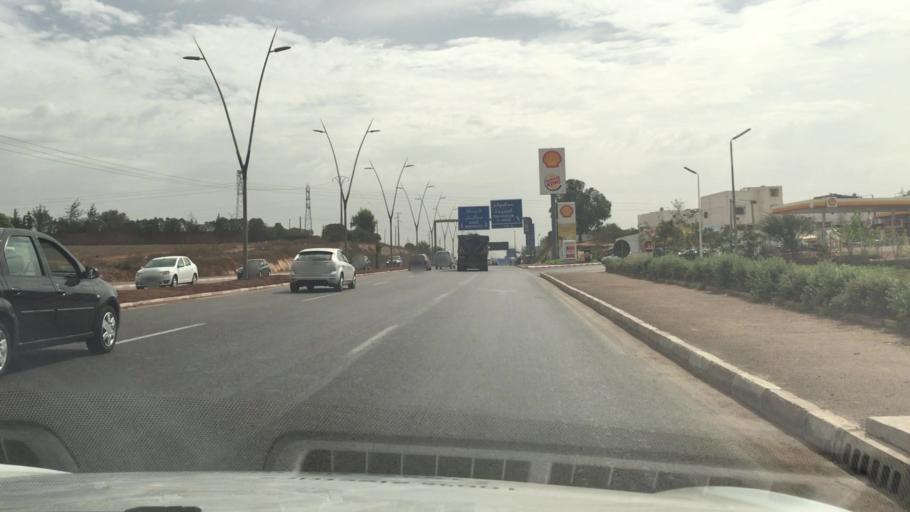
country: MA
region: Grand Casablanca
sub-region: Nouaceur
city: Bouskoura
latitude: 33.5078
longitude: -7.6300
